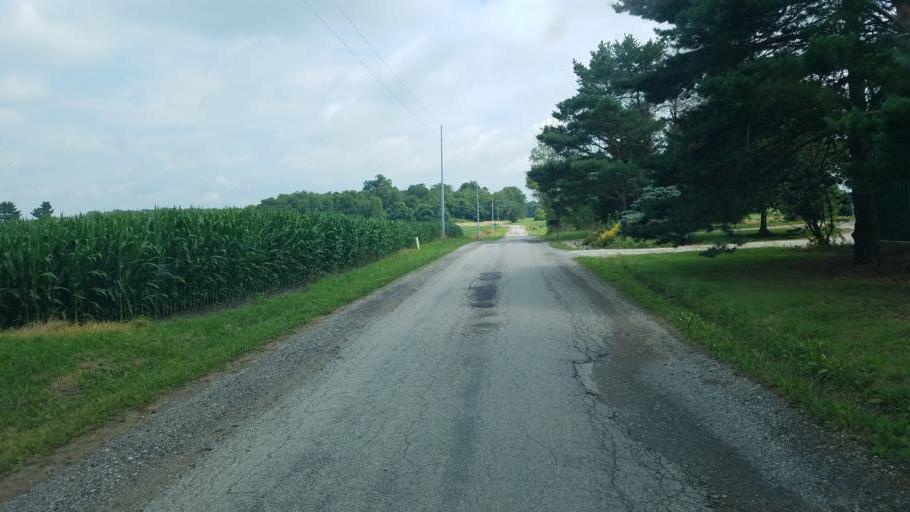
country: US
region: Ohio
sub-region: Knox County
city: Centerburg
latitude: 40.2910
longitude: -82.5866
